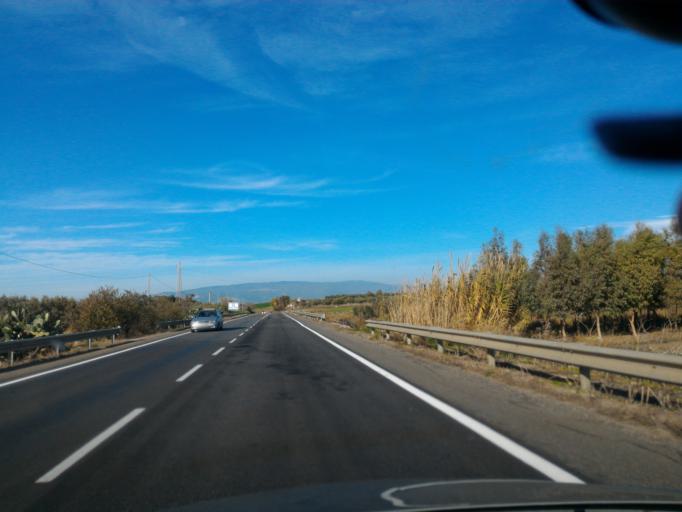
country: IT
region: Calabria
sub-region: Provincia di Crotone
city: Le Castella
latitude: 38.9361
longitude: 17.0046
